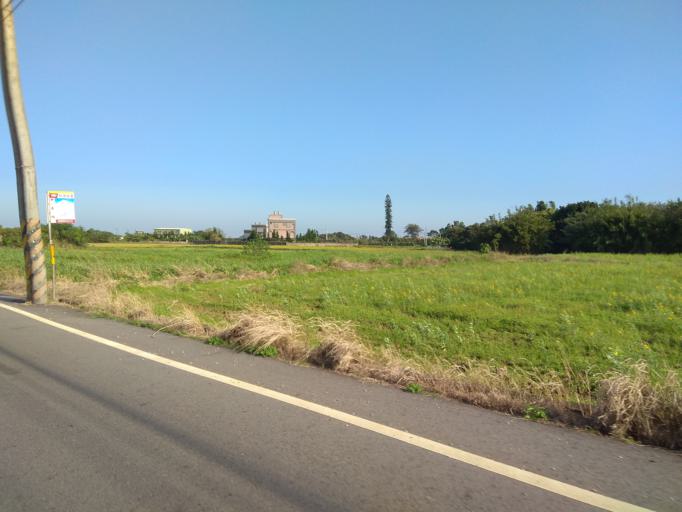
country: TW
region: Taiwan
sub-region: Hsinchu
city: Zhubei
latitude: 24.9882
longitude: 121.0751
